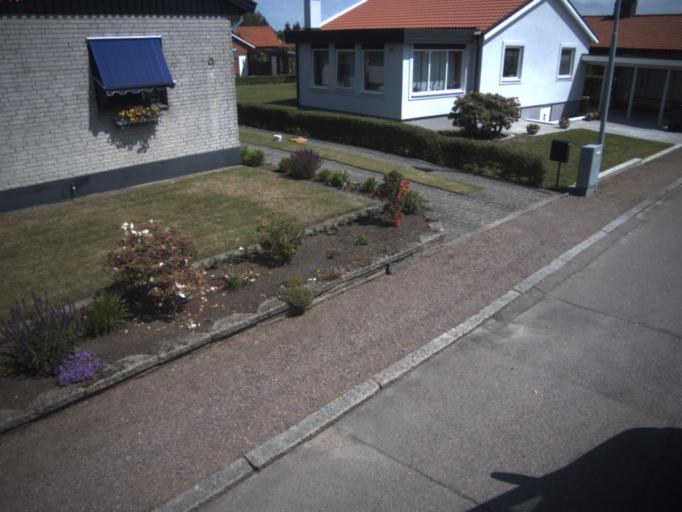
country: SE
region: Skane
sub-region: Helsingborg
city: Helsingborg
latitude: 56.0449
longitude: 12.7356
